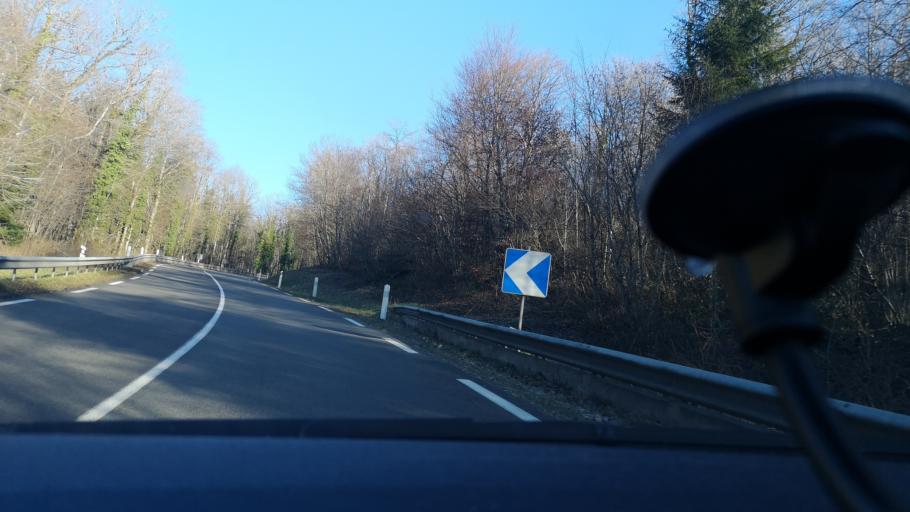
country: FR
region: Franche-Comte
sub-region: Departement du Jura
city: Poligny
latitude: 46.8159
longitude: 5.7694
